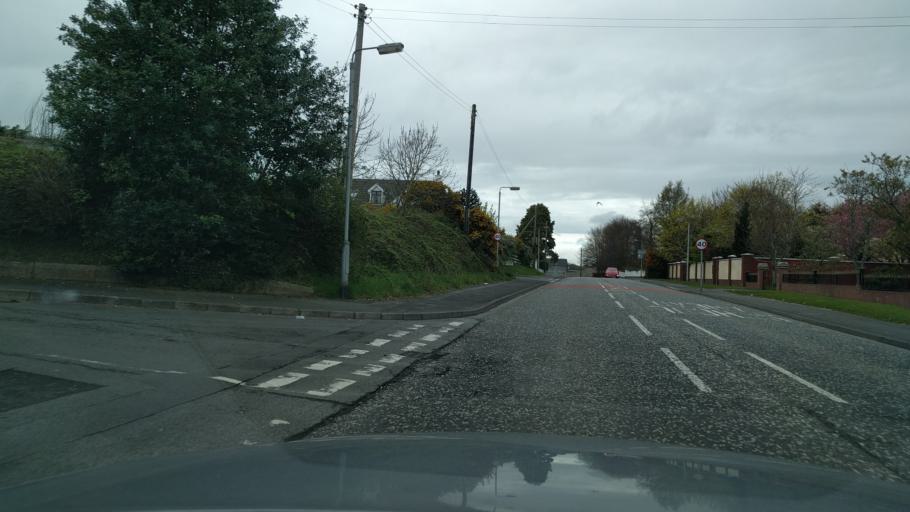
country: GB
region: Northern Ireland
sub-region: Down District
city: Warrenpoint
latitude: 54.1100
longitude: -6.2566
